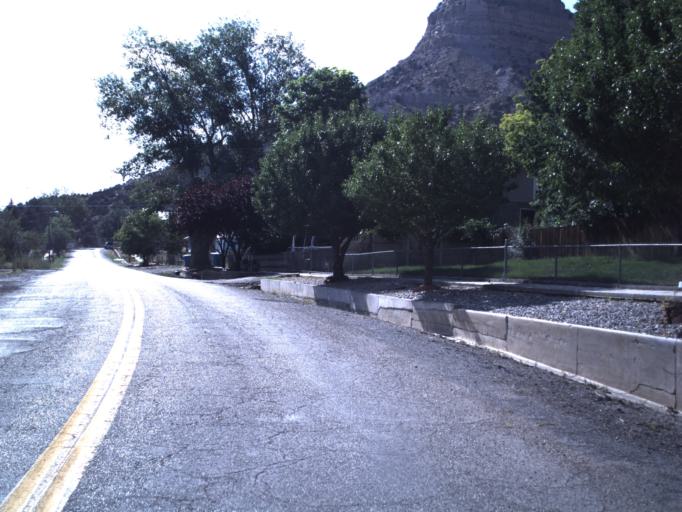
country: US
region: Utah
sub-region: Carbon County
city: Helper
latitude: 39.6884
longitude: -110.8055
